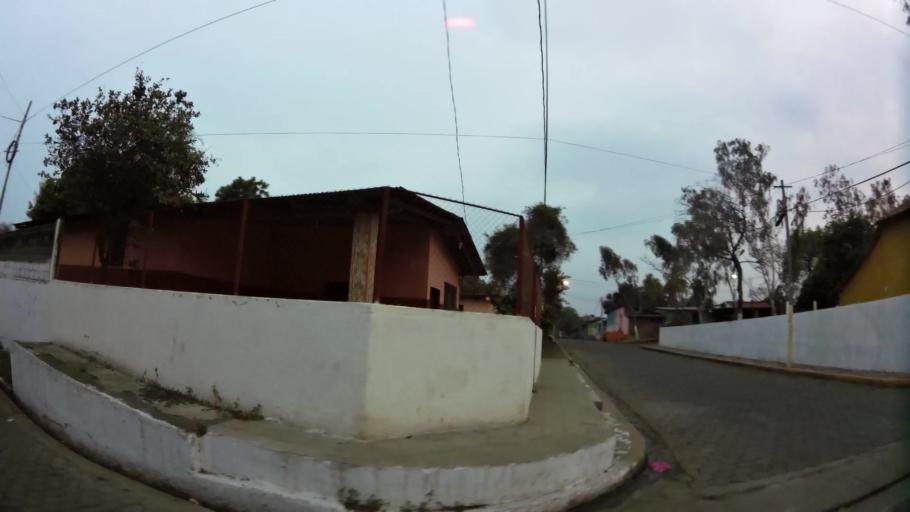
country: NI
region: Masaya
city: Nindiri
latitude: 12.0035
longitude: -86.1192
